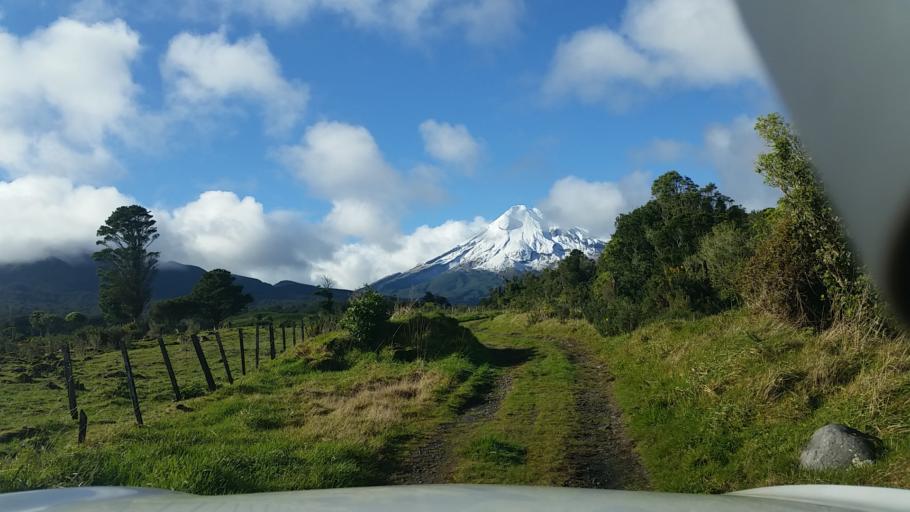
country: NZ
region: Taranaki
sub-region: South Taranaki District
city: Opunake
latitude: -39.2504
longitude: 173.9458
